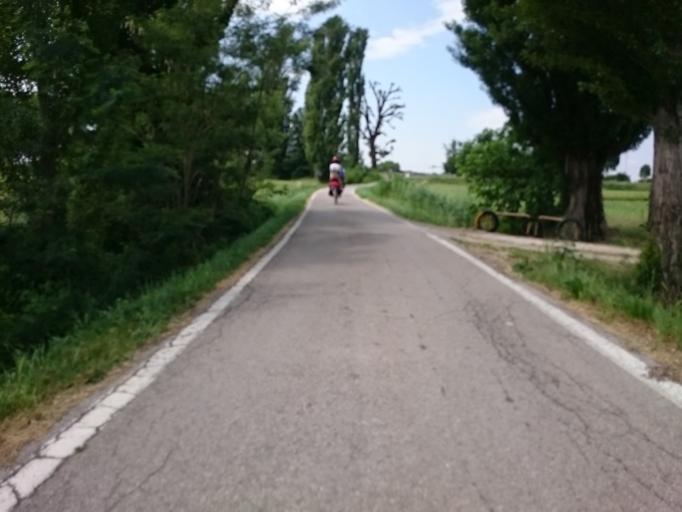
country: IT
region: Veneto
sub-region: Provincia di Padova
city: Carceri
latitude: 45.1875
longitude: 11.6319
